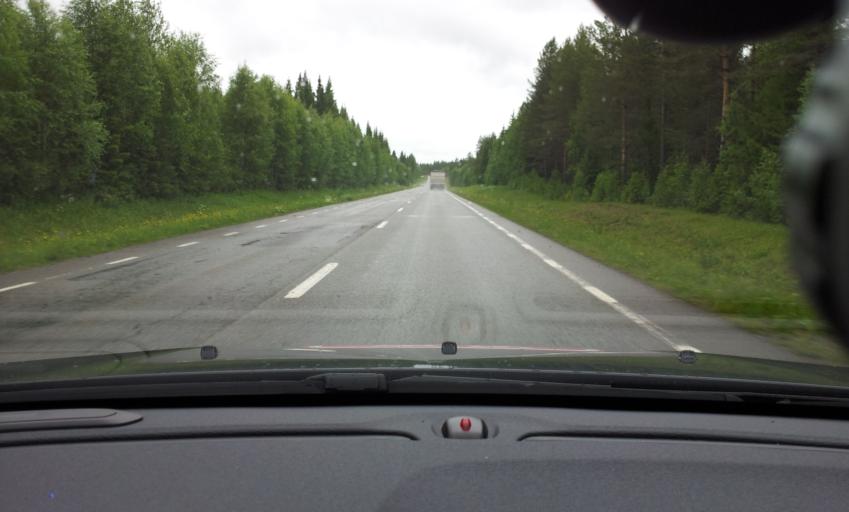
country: SE
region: Jaemtland
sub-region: OEstersunds Kommun
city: Lit
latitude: 63.6238
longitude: 14.6733
